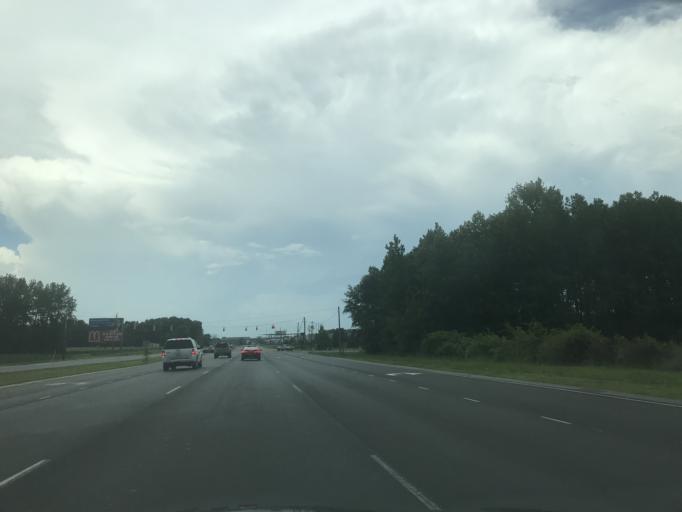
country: US
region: North Carolina
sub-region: Johnston County
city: Clayton
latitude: 35.6074
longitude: -78.4163
